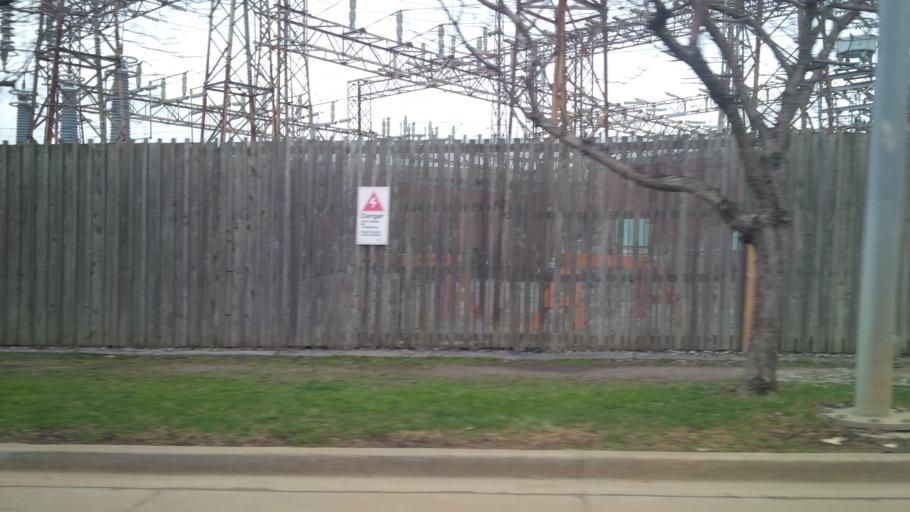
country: CA
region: Ontario
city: Toronto
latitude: 43.6365
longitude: -79.4116
